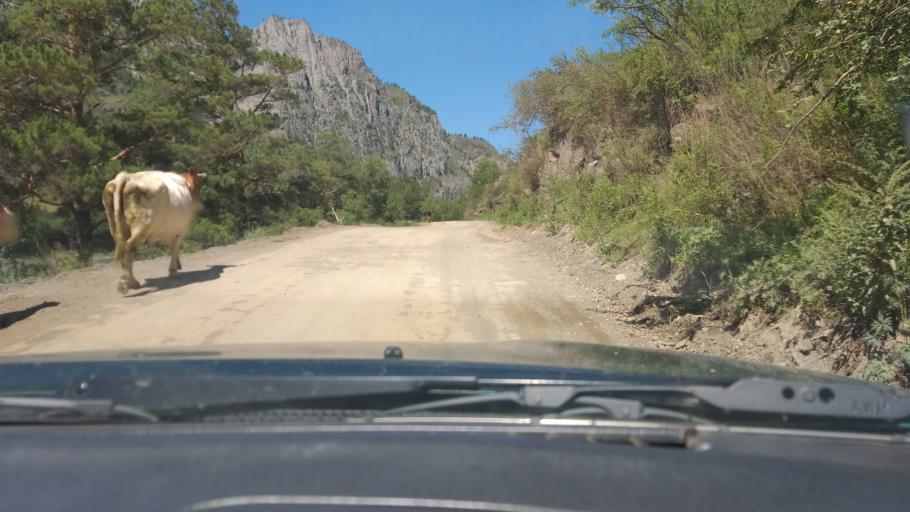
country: RU
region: Altay
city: Chemal
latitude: 51.2025
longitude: 86.0855
